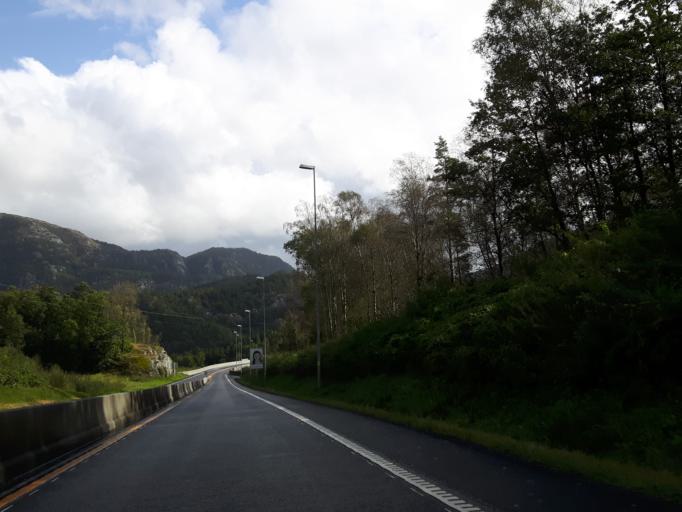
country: NO
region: Vest-Agder
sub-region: Flekkefjord
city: Flekkefjord
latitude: 58.2751
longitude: 6.8058
